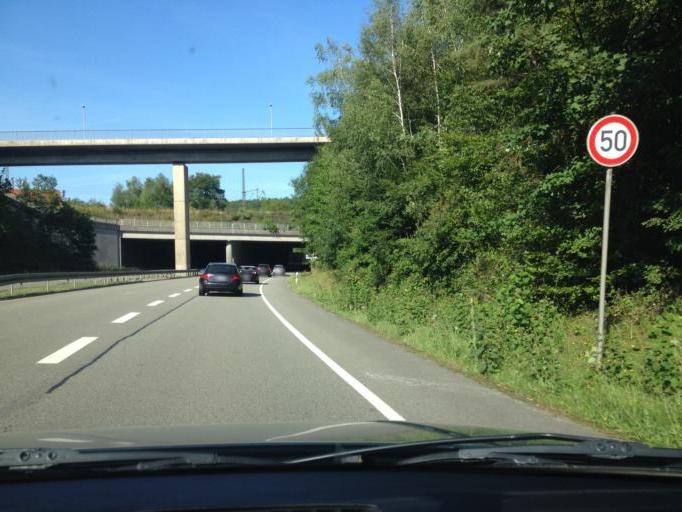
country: DE
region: Saarland
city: Schiffweiler
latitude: 49.3489
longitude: 7.1465
